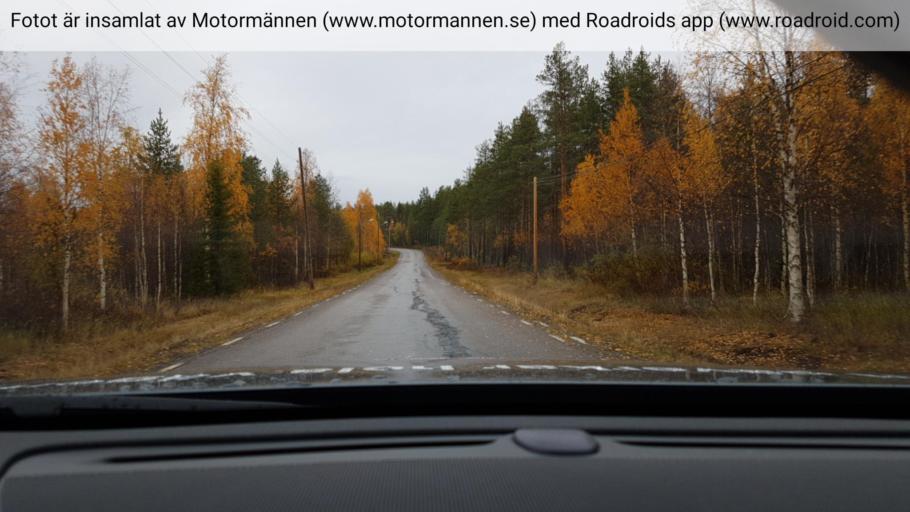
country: SE
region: Norrbotten
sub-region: Pajala Kommun
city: Pajala
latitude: 67.1476
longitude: 22.6531
